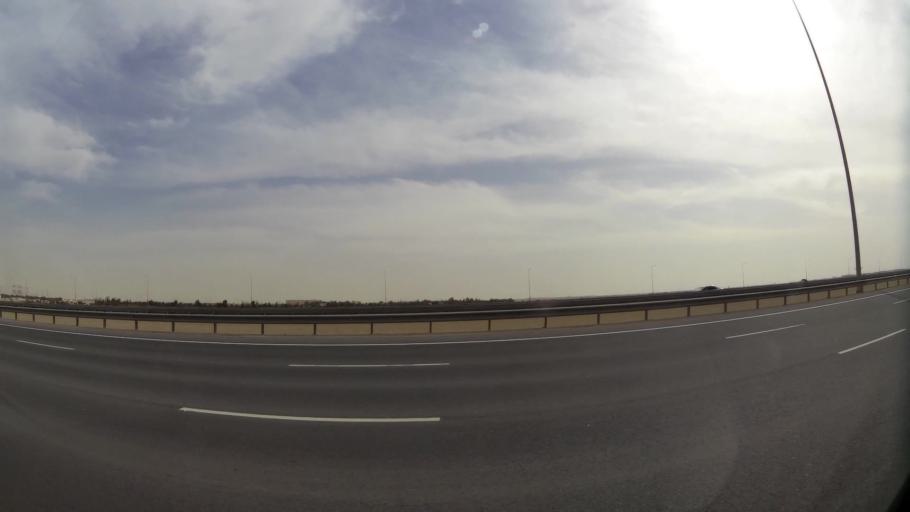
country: QA
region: Baladiyat ar Rayyan
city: Ash Shahaniyah
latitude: 25.3509
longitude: 51.2970
